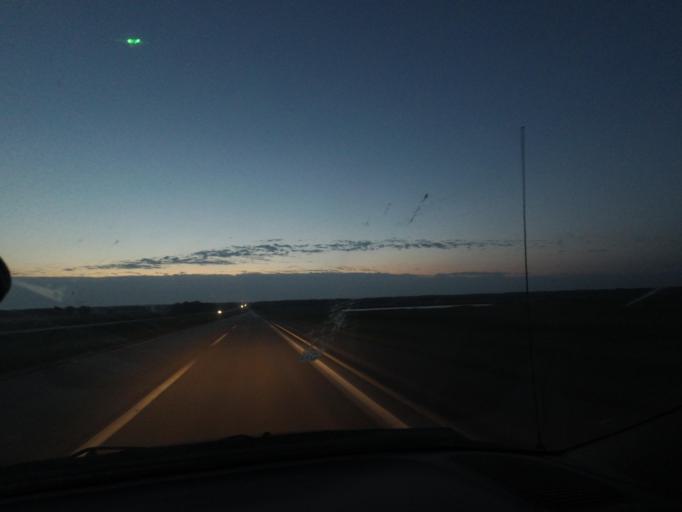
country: US
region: Missouri
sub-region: Linn County
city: Linneus
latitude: 39.7773
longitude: -93.3433
